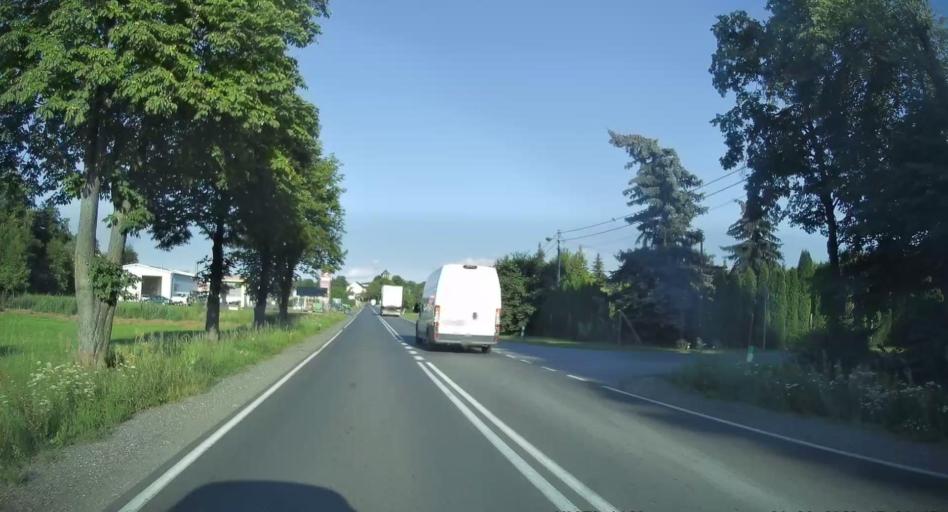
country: PL
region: Masovian Voivodeship
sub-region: Powiat grojecki
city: Bledow
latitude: 51.8012
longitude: 20.6159
